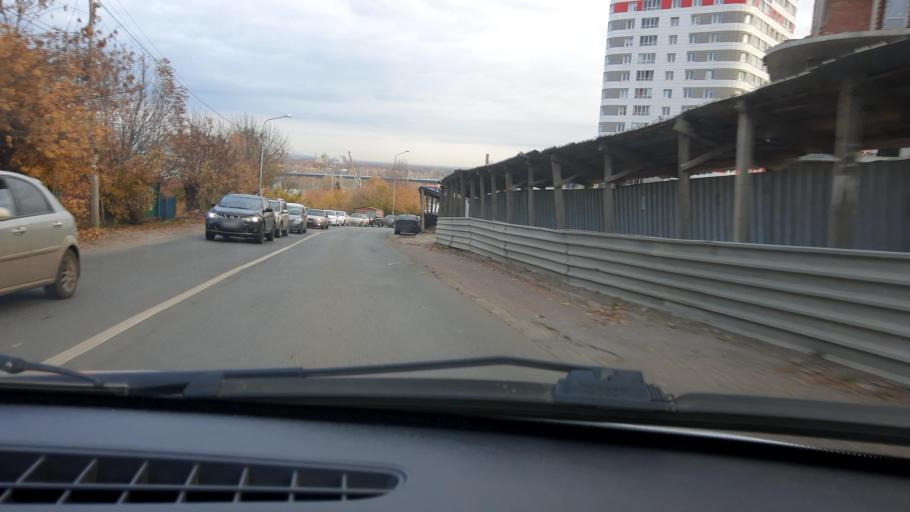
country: RU
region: Bashkortostan
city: Ufa
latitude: 54.7489
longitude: 55.9651
